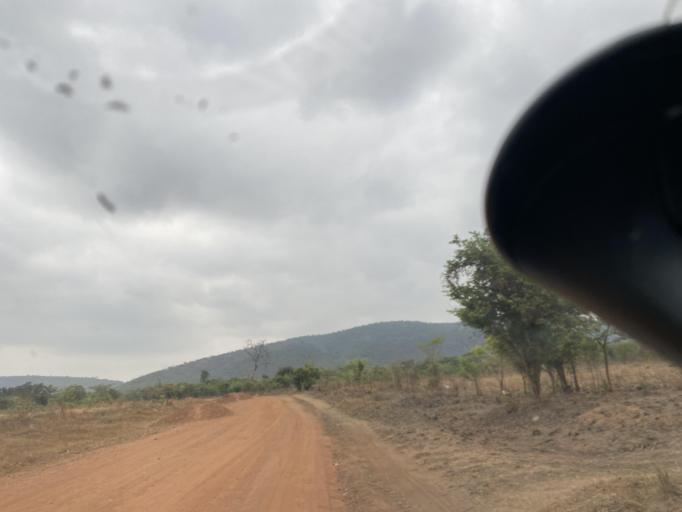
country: ZM
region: Lusaka
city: Chongwe
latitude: -15.1960
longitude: 28.7658
